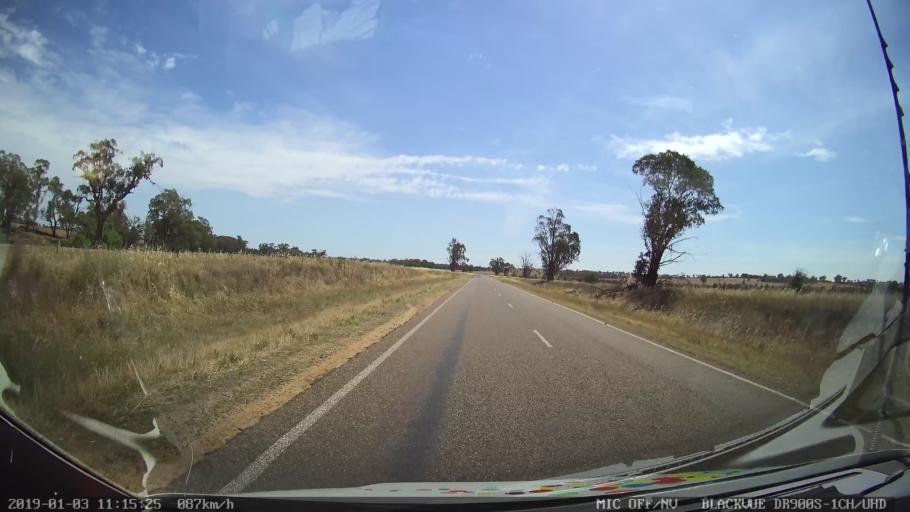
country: AU
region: New South Wales
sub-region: Young
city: Young
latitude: -34.1641
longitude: 148.2645
